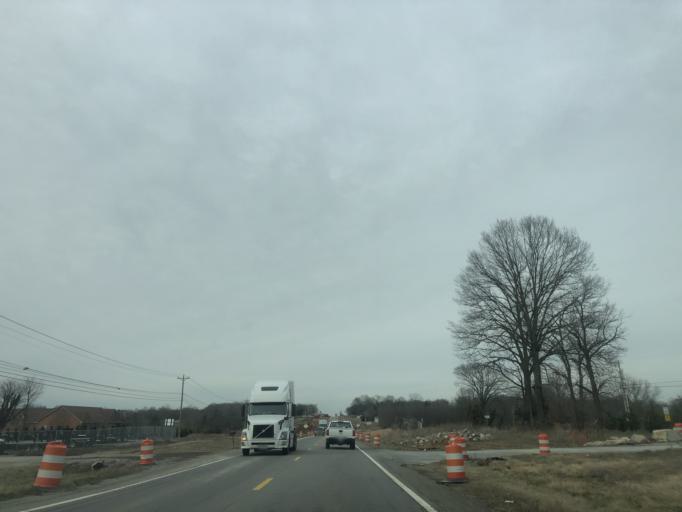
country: US
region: Tennessee
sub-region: Wilson County
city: Mount Juliet
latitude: 36.2657
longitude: -86.4403
